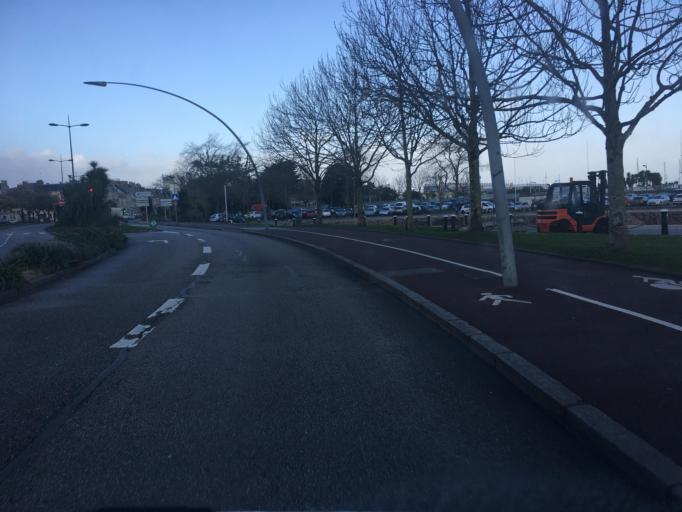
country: FR
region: Lower Normandy
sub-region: Departement de la Manche
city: Cherbourg-Octeville
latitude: 49.6420
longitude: -1.6216
